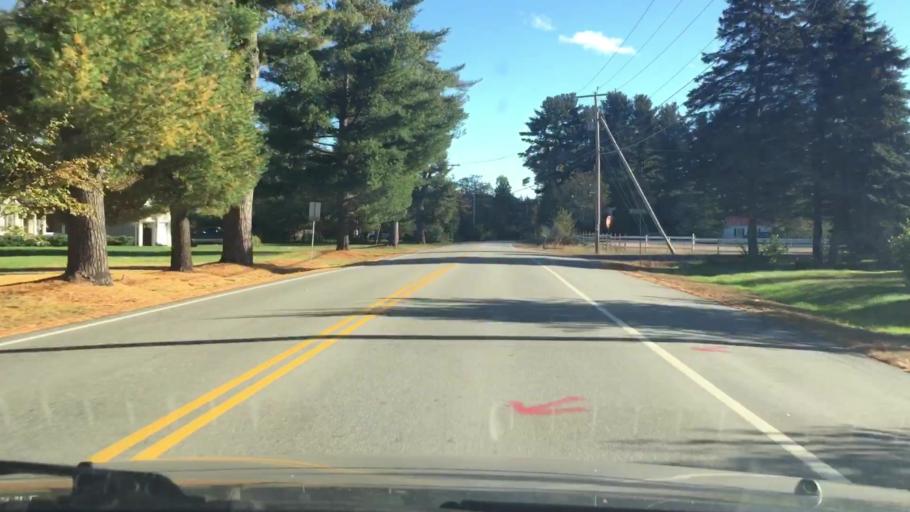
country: US
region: New Hampshire
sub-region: Cheshire County
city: Swanzey
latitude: 42.8541
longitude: -72.2779
